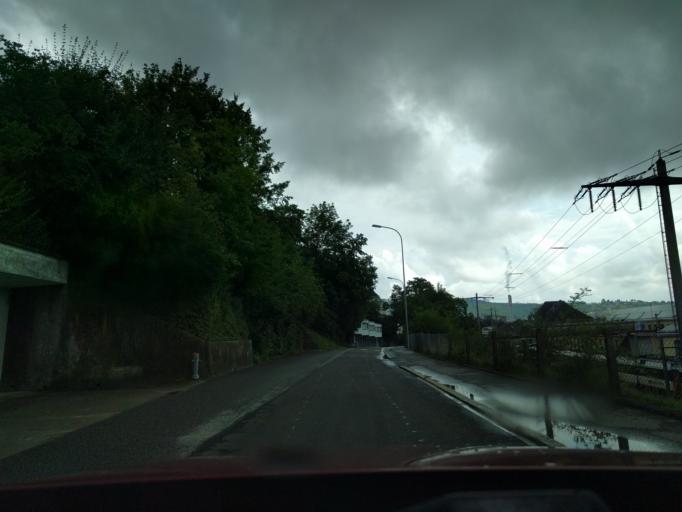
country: CH
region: Bern
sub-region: Biel/Bienne District
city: Biel/Bienne
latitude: 47.1323
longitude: 7.2585
